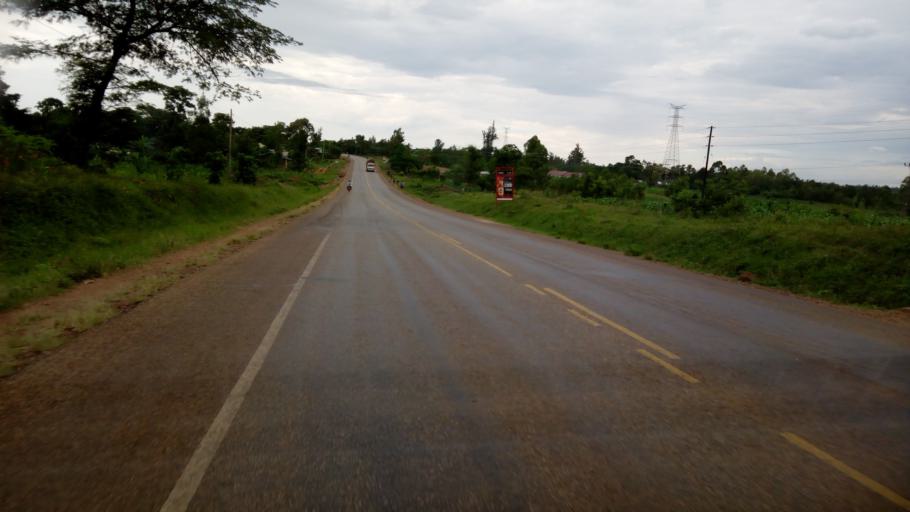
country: UG
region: Eastern Region
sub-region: Mbale District
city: Mbale
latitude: 1.0004
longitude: 34.1676
